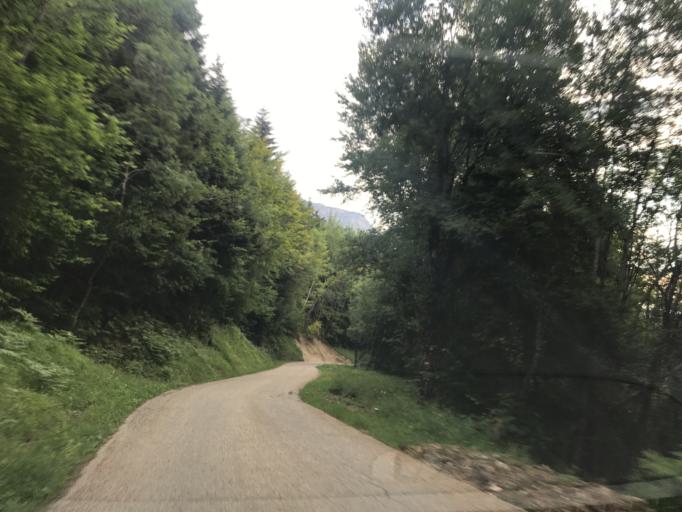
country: FR
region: Rhone-Alpes
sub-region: Departement de l'Isere
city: Le Touvet
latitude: 45.3650
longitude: 5.9206
